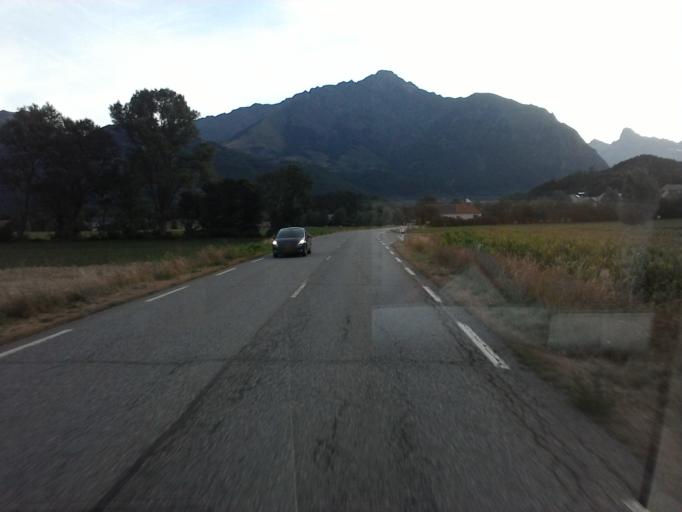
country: FR
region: Provence-Alpes-Cote d'Azur
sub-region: Departement des Hautes-Alpes
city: Saint-Bonnet-en-Champsaur
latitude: 44.7615
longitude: 6.0101
